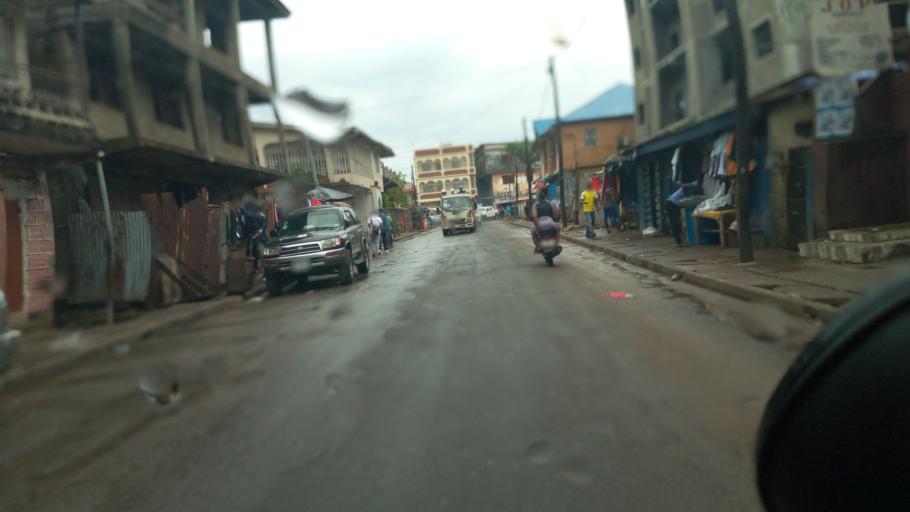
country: SL
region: Western Area
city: Freetown
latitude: 8.4766
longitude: -13.2389
